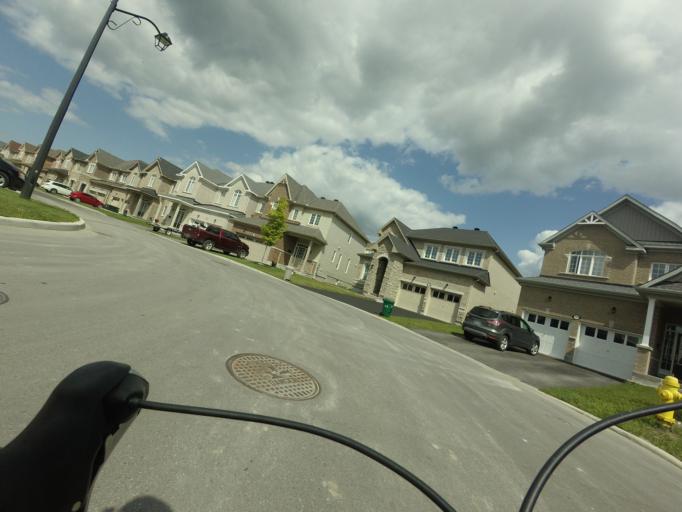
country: CA
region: Ontario
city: Bells Corners
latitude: 45.2759
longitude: -75.8451
